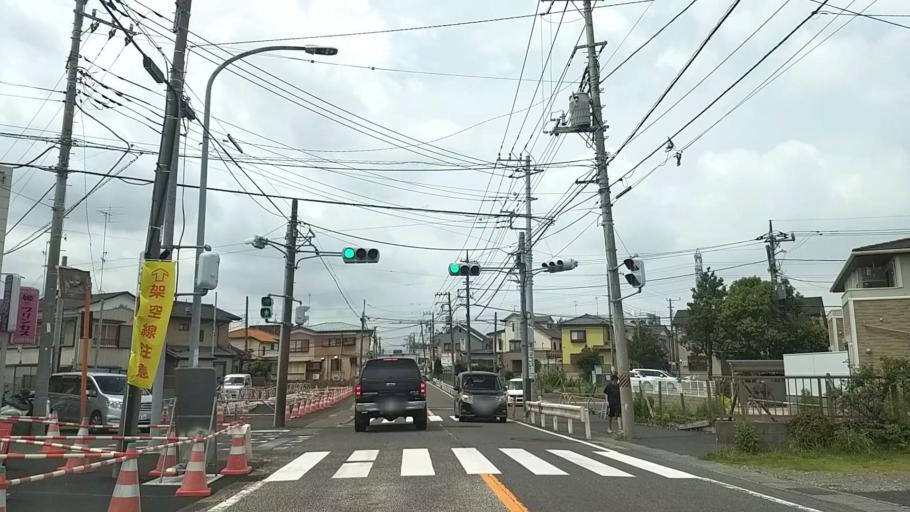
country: JP
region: Kanagawa
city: Minami-rinkan
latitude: 35.4508
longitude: 139.4697
